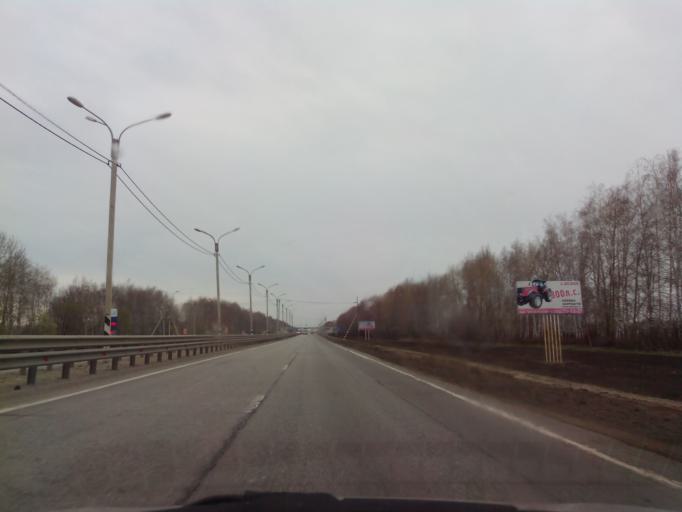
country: RU
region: Tambov
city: Selezni
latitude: 52.7575
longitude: 41.1494
